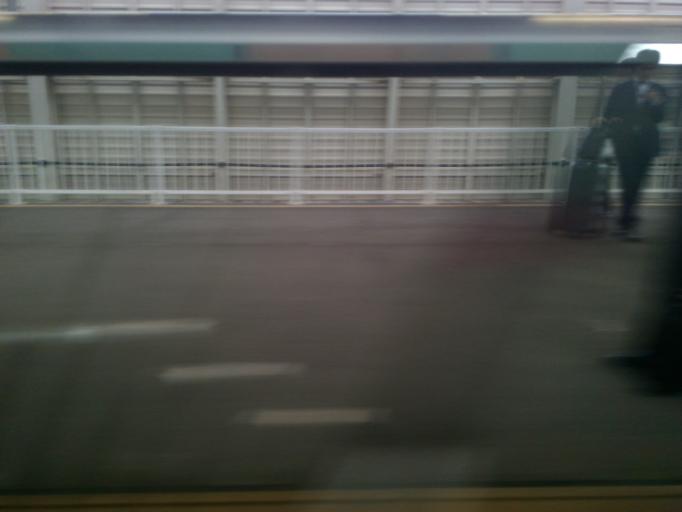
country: JP
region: Miyagi
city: Furukawa
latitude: 38.5717
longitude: 140.9682
